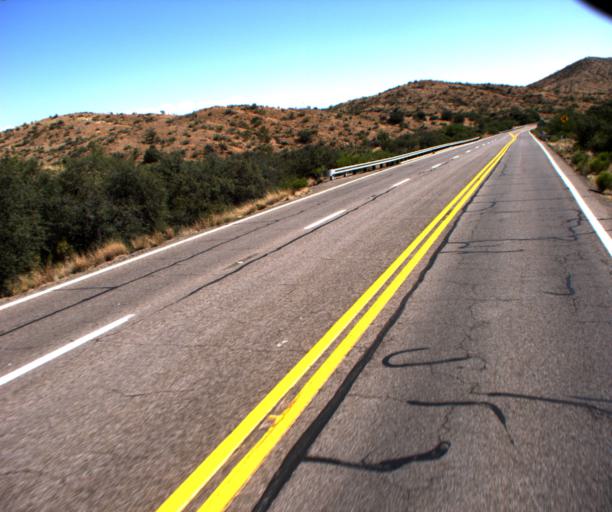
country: US
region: Arizona
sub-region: Pinal County
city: Oracle
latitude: 32.6292
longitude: -110.7418
